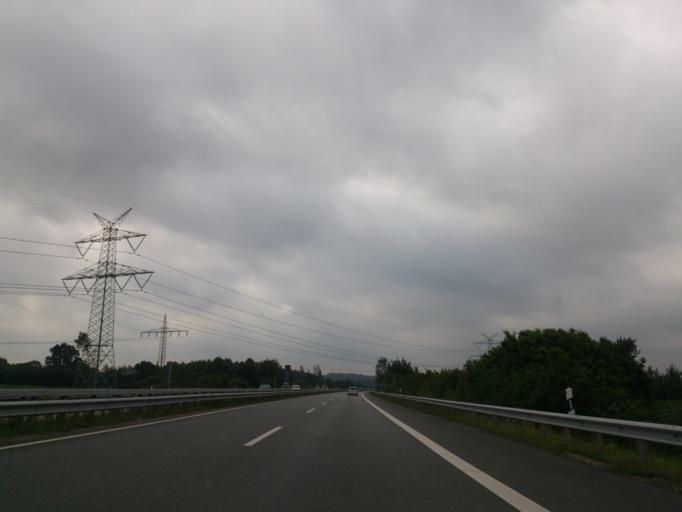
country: DE
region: Schleswig-Holstein
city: Kaisborstel
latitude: 54.0027
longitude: 9.4810
